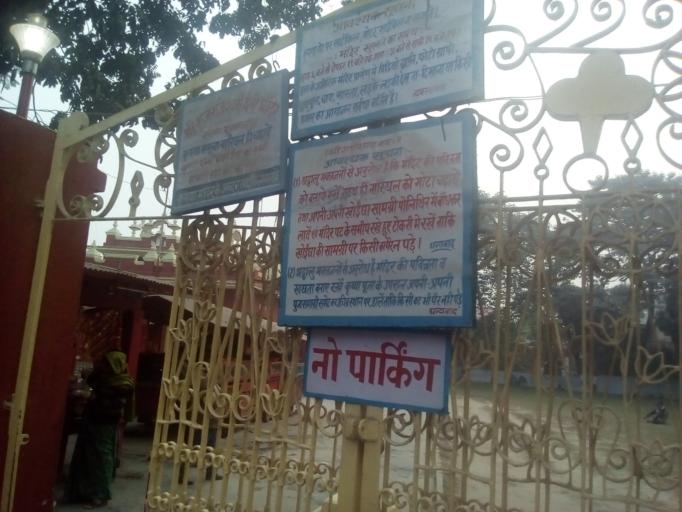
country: IN
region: Bihar
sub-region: Muzaffarpur
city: Muzaffarpur
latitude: 26.1163
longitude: 85.3938
